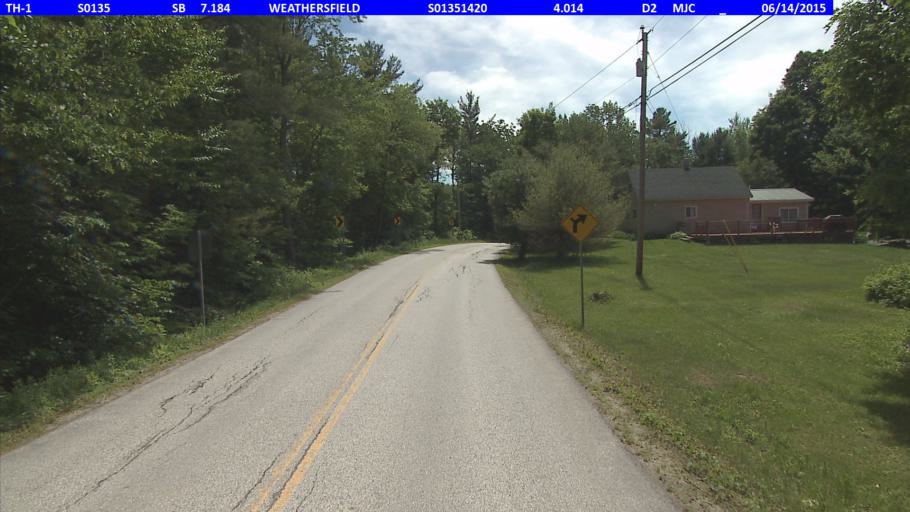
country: US
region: Vermont
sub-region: Windsor County
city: Springfield
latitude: 43.3979
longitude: -72.4619
